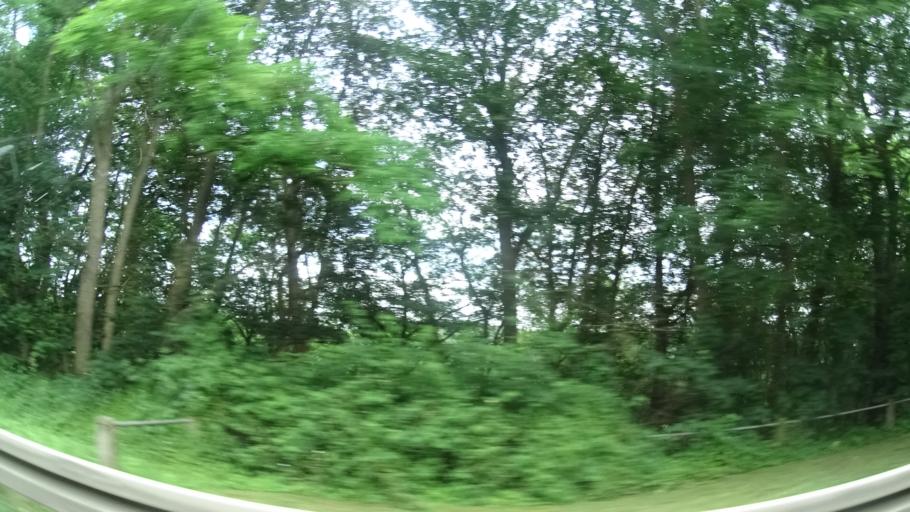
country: DE
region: Hesse
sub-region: Regierungsbezirk Kassel
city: Bad Arolsen
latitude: 51.3870
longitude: 9.0618
